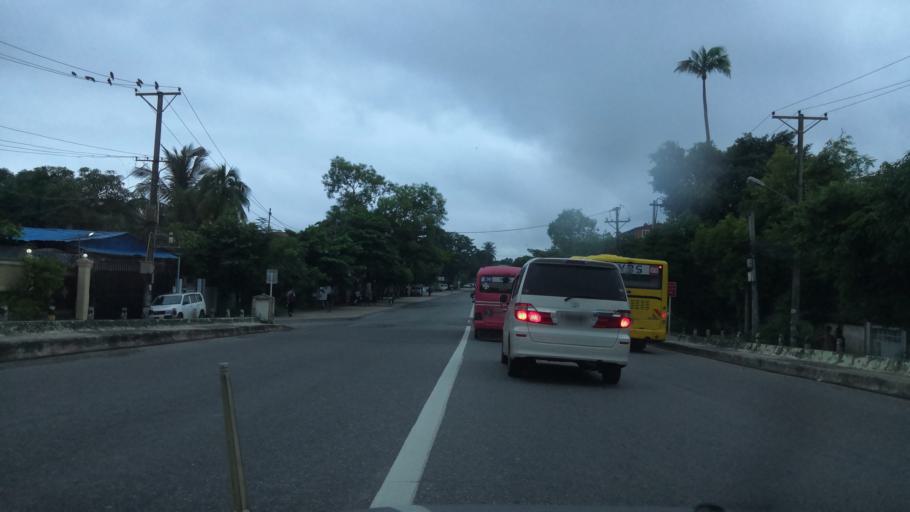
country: MM
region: Yangon
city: Yangon
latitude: 16.8514
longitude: 96.1635
